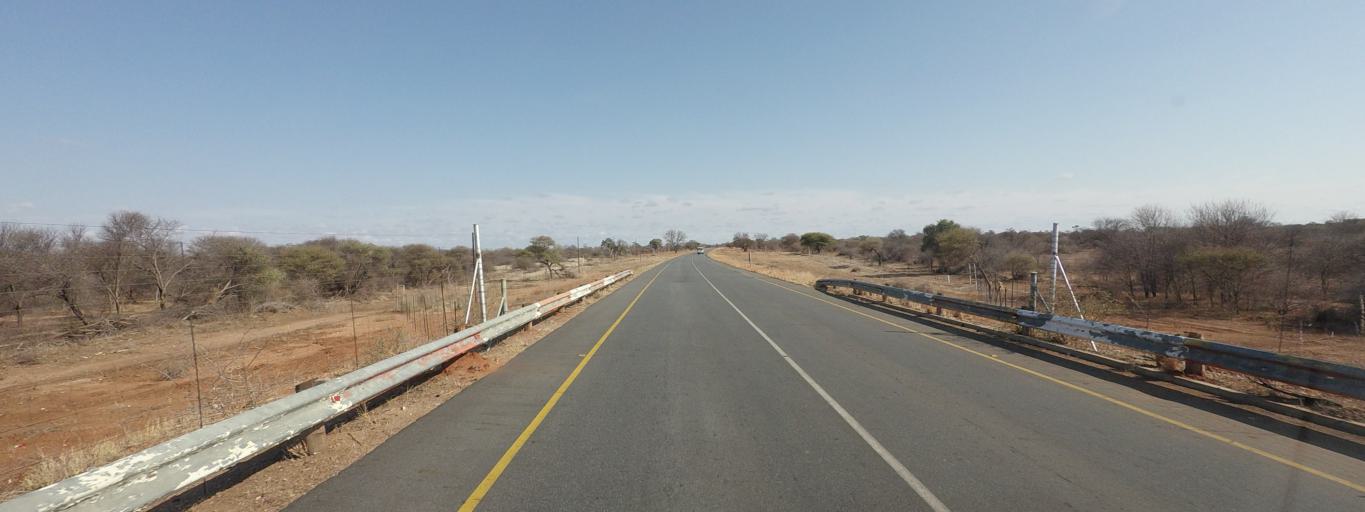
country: BW
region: Central
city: Makobeng
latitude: -22.9516
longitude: 27.8975
